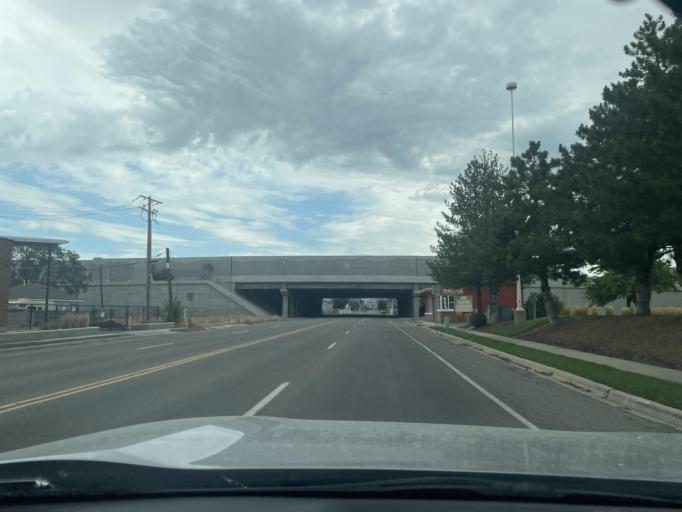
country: US
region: Utah
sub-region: Salt Lake County
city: South Salt Lake
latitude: 40.7170
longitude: -111.8911
